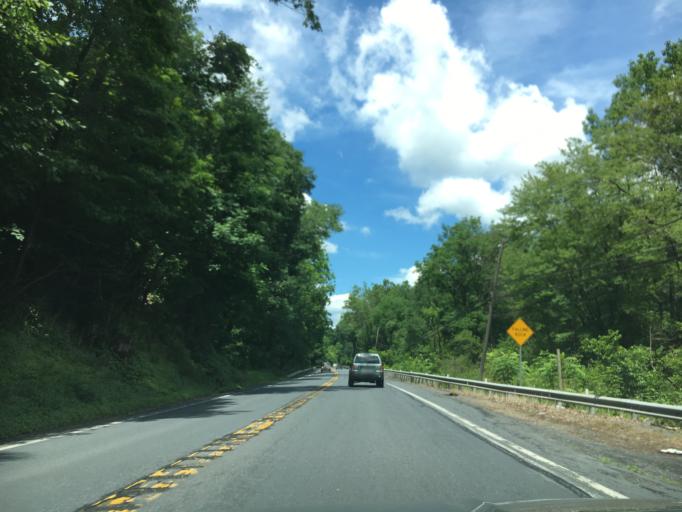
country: US
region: Pennsylvania
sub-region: Lehigh County
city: Laurys Station
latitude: 40.7101
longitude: -75.5220
